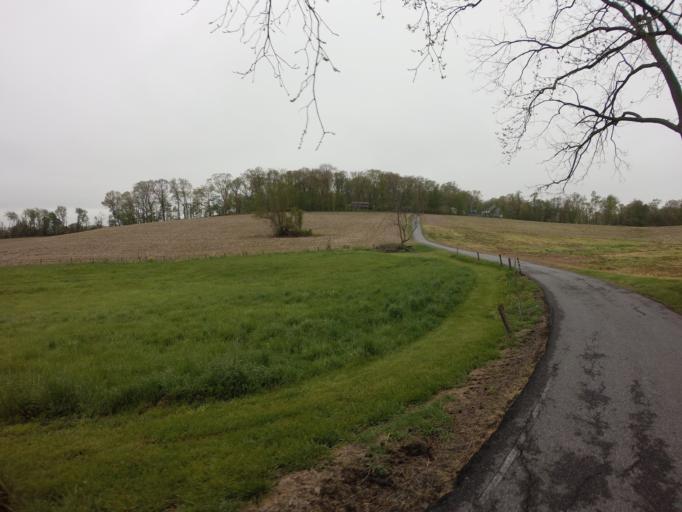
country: US
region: Maryland
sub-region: Carroll County
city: Hampstead
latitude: 39.5781
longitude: -76.7661
